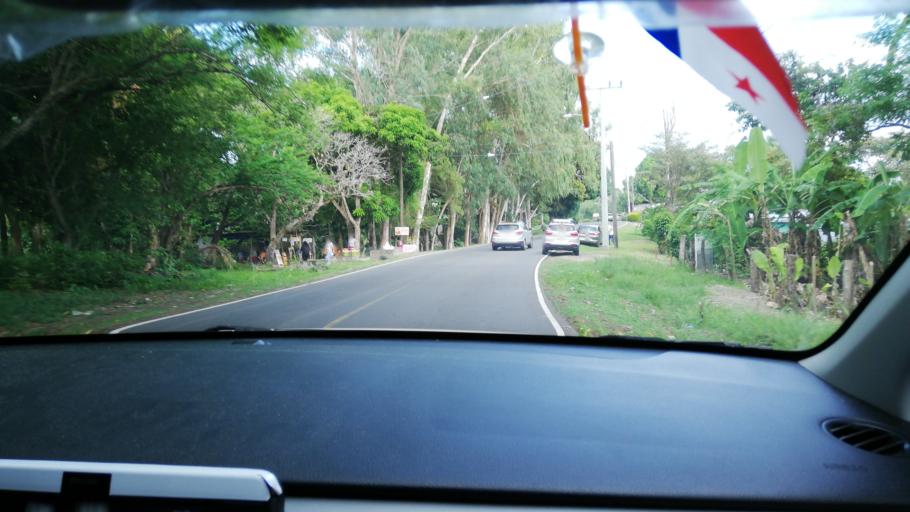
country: PA
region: Panama
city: Las Colinas
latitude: 8.5234
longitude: -80.0380
